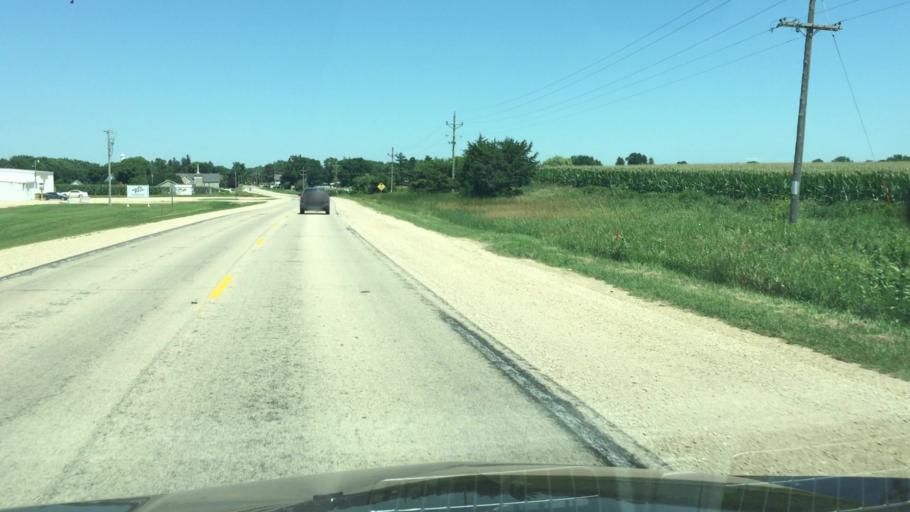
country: US
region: Iowa
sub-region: Cedar County
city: Mechanicsville
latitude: 41.9877
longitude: -91.1418
